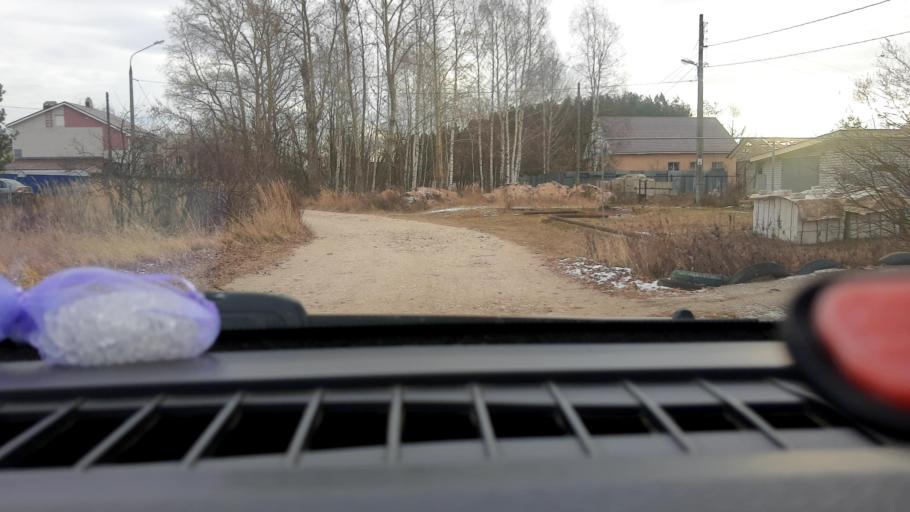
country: RU
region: Nizjnij Novgorod
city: Gorbatovka
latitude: 56.3817
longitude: 43.7764
